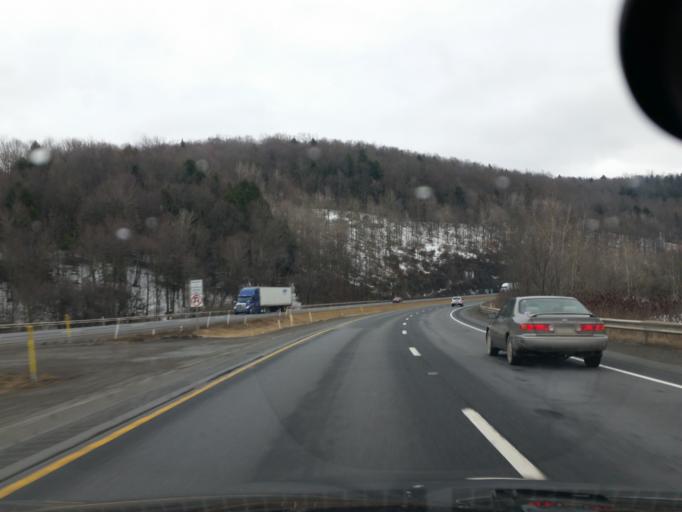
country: US
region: Pennsylvania
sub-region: Wyoming County
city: Factoryville
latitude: 41.7020
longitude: -75.6692
